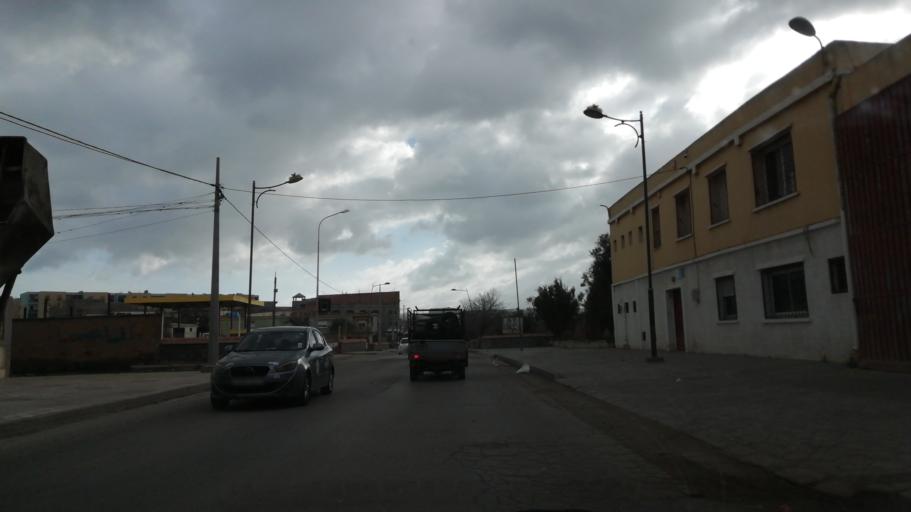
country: DZ
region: Oran
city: Sidi ech Chahmi
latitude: 35.6570
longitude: -0.5278
